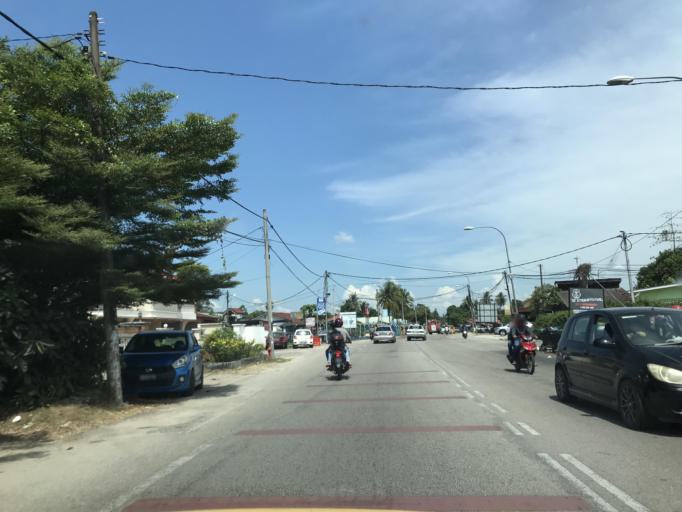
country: MY
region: Kelantan
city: Kota Bharu
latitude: 6.1182
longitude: 102.1949
